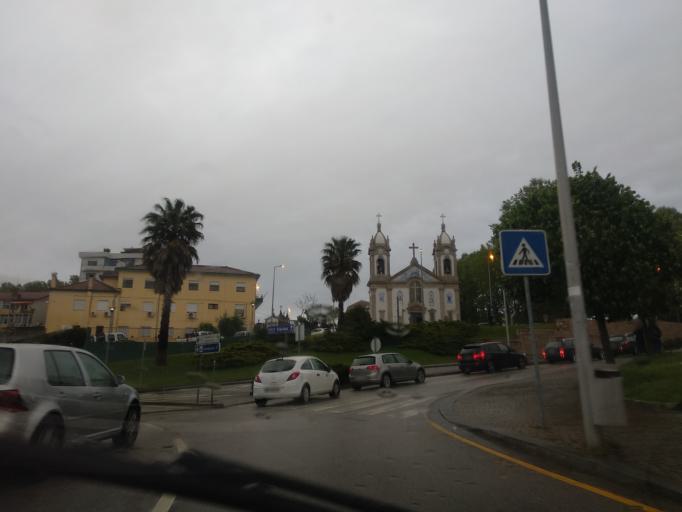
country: PT
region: Porto
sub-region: Gondomar
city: Rio Tinto
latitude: 41.1777
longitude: -8.5606
